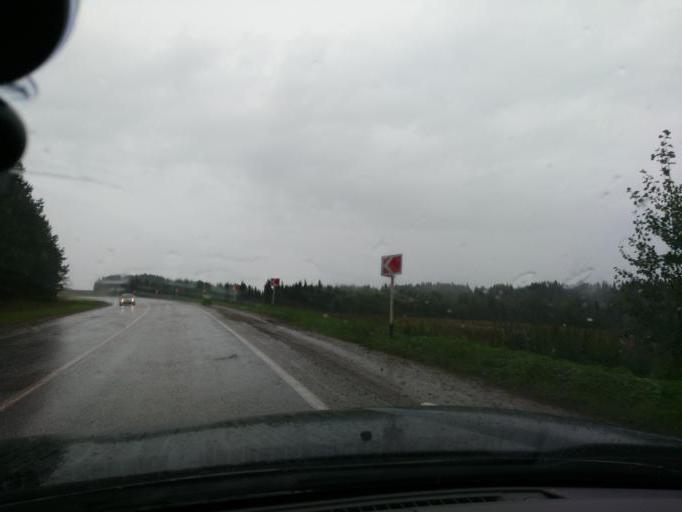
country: RU
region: Perm
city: Osa
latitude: 57.3063
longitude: 55.6200
